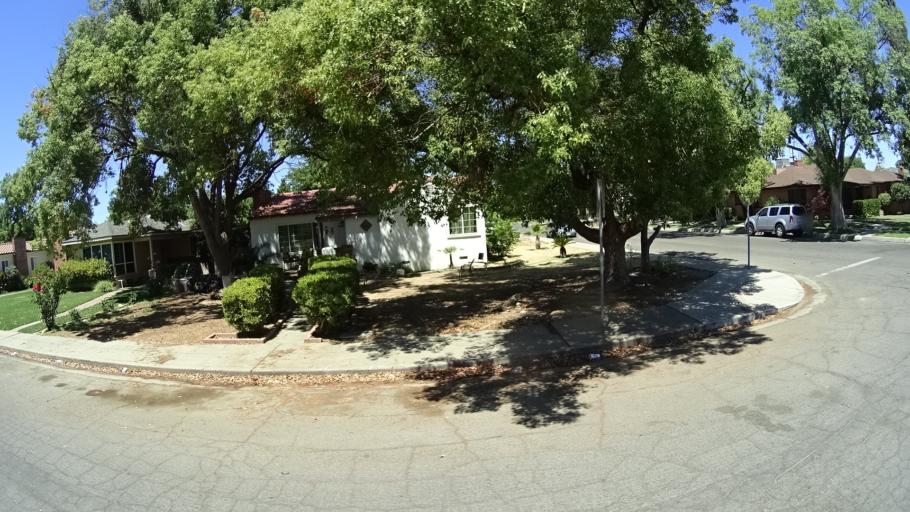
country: US
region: California
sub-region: Fresno County
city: Fresno
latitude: 36.7756
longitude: -119.8142
